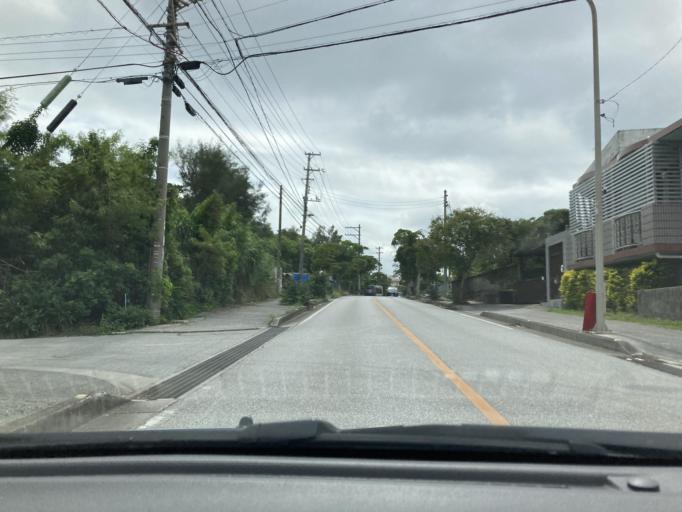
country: JP
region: Okinawa
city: Ginowan
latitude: 26.2709
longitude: 127.7783
